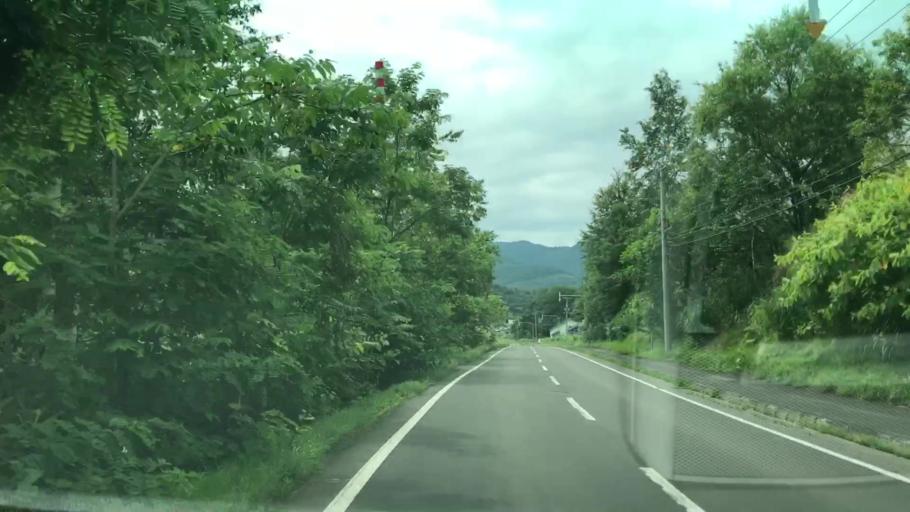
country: JP
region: Hokkaido
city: Yoichi
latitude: 43.0648
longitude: 140.8210
